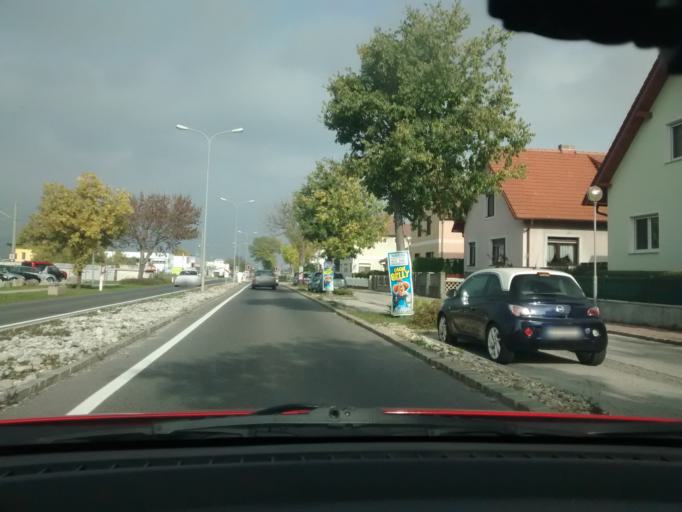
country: AT
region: Lower Austria
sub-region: Politischer Bezirk Baden
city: Traiskirchen
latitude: 48.0240
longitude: 16.2987
